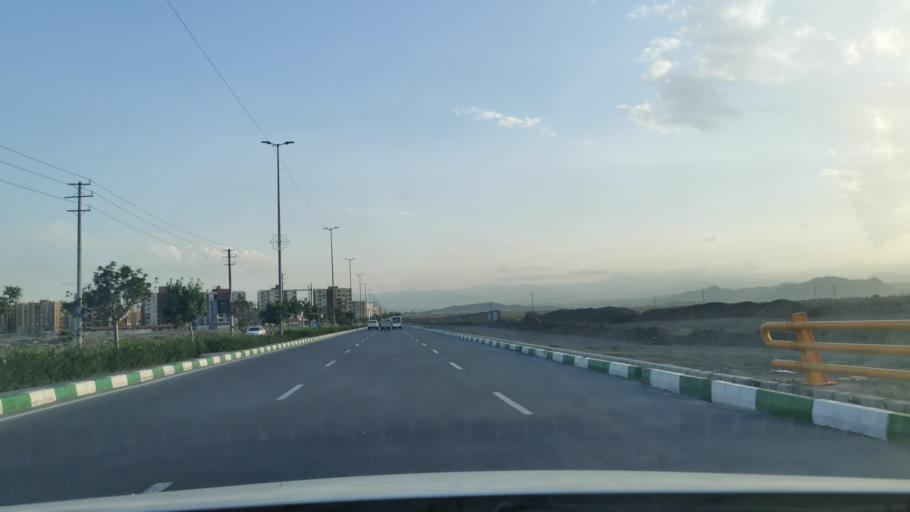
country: IR
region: Razavi Khorasan
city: Mashhad
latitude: 36.3980
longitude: 59.4765
